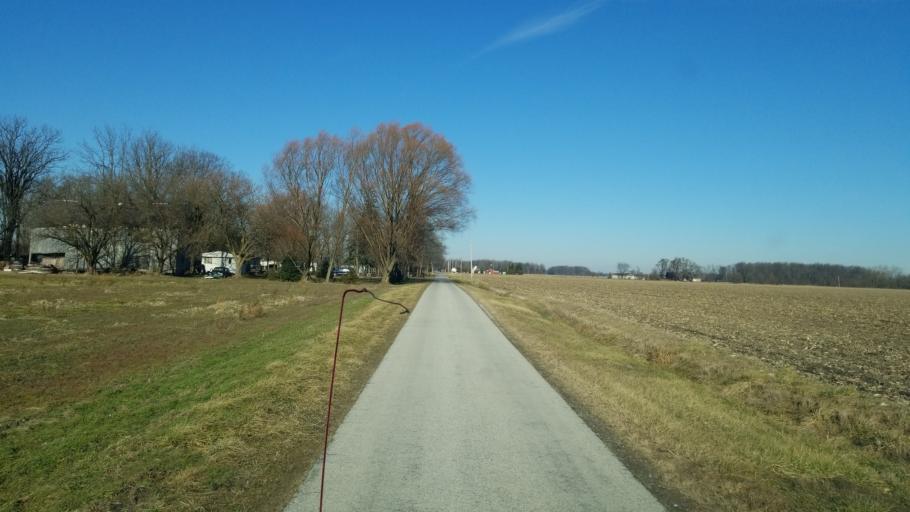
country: US
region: Ohio
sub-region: Henry County
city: Liberty Center
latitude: 41.3653
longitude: -83.9802
